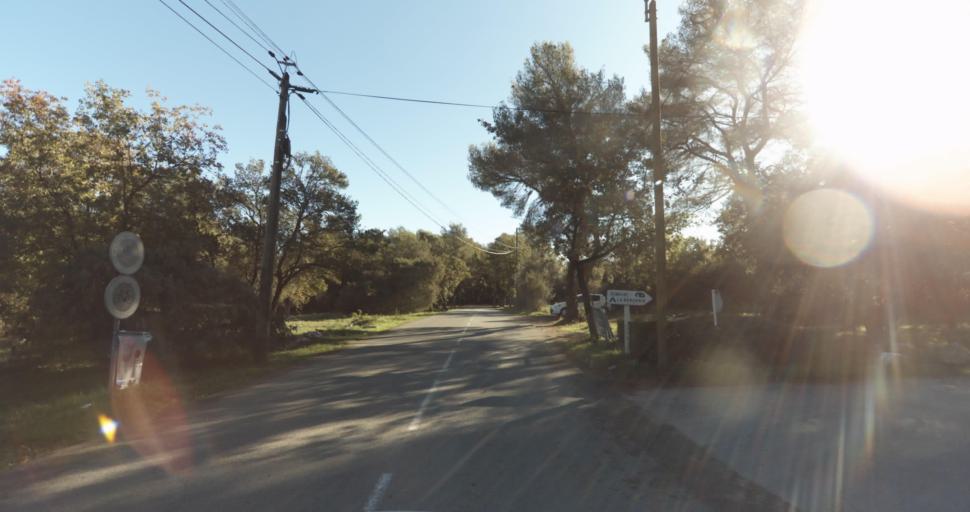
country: FR
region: Provence-Alpes-Cote d'Azur
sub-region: Departement des Alpes-Maritimes
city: Vence
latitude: 43.7133
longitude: 7.0896
